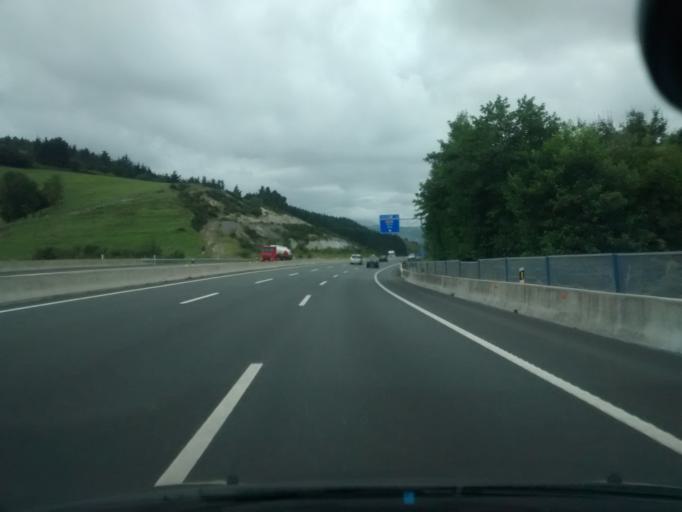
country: ES
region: Basque Country
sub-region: Provincia de Guipuzcoa
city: Orio
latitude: 43.2859
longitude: -2.0962
